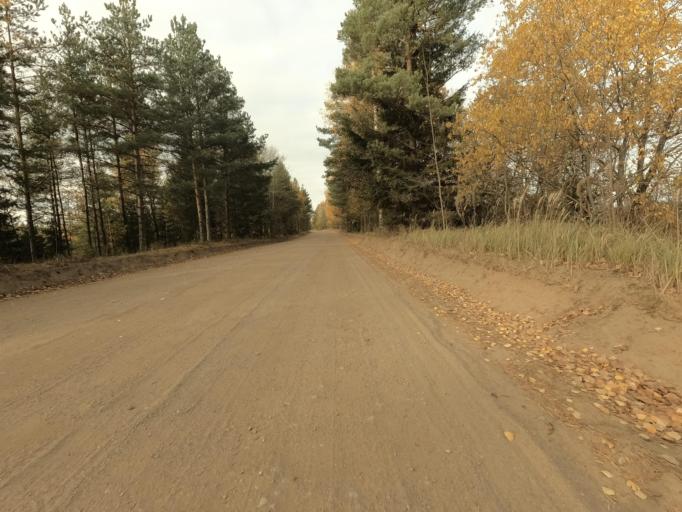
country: RU
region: Leningrad
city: Priladozhskiy
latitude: 59.6756
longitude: 31.3661
